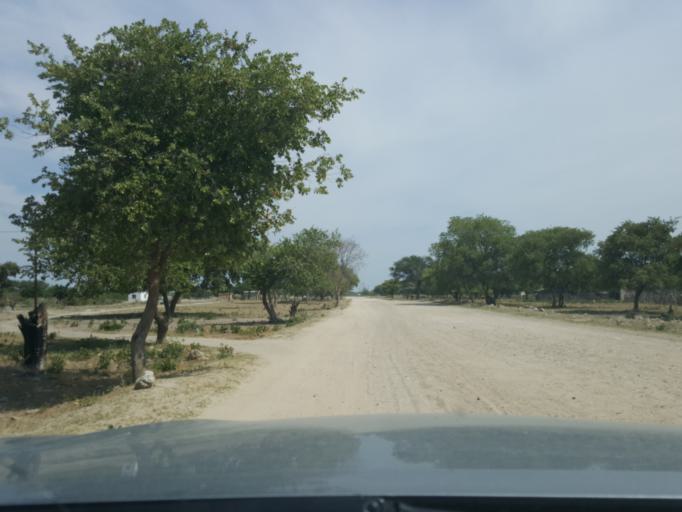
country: BW
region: North West
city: Shakawe
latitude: -18.3105
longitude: 21.8941
